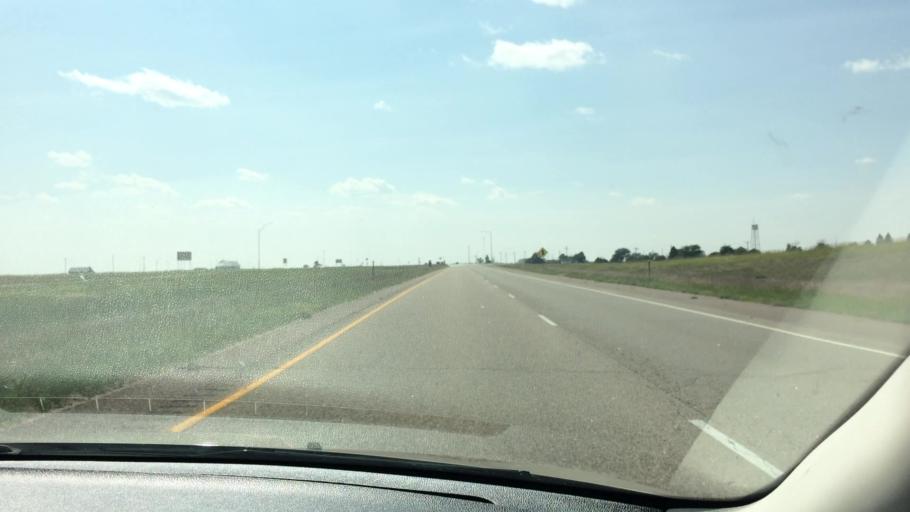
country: US
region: Colorado
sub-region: Lincoln County
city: Hugo
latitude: 39.2751
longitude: -103.4931
